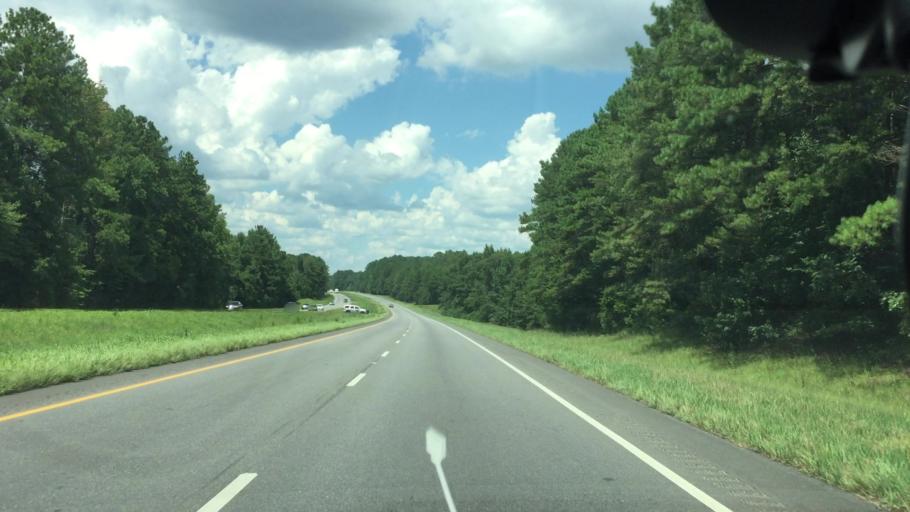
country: US
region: Alabama
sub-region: Pike County
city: Troy
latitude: 31.9071
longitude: -86.0116
